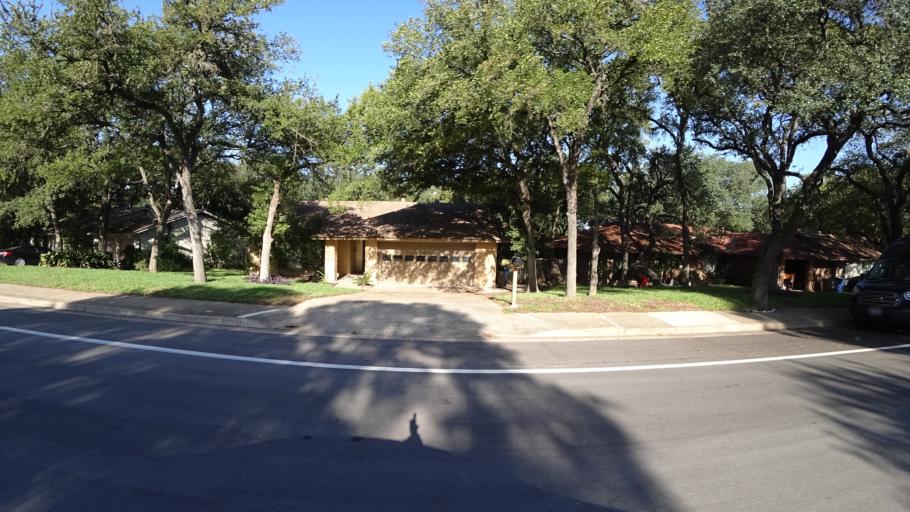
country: US
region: Texas
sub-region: Travis County
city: Shady Hollow
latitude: 30.2089
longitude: -97.8113
